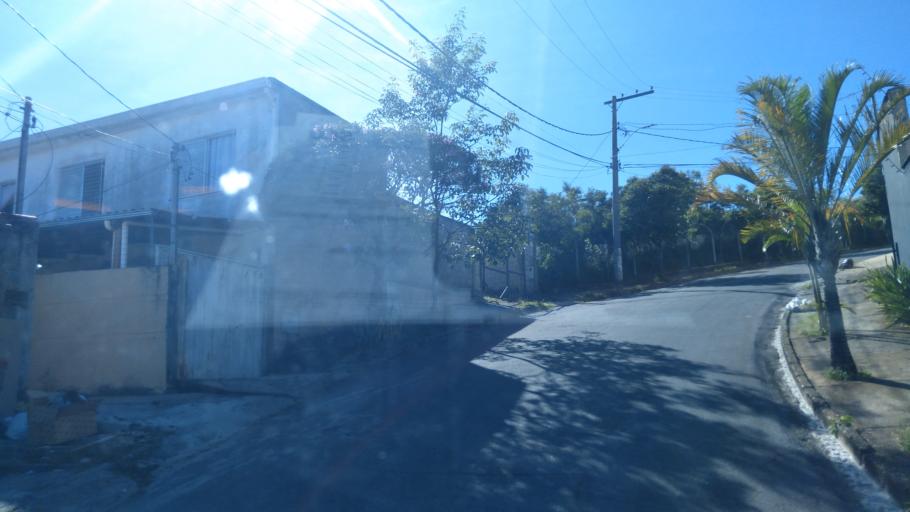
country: BR
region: Minas Gerais
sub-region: Belo Horizonte
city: Belo Horizonte
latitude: -19.9205
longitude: -43.8924
